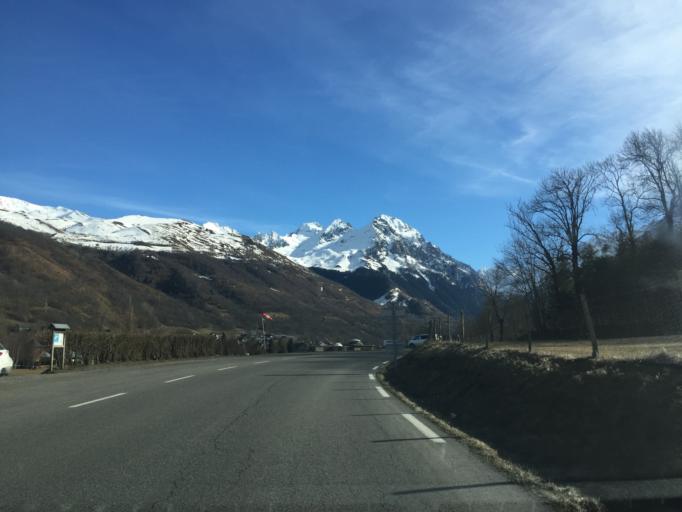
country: FR
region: Midi-Pyrenees
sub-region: Departement des Hautes-Pyrenees
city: Saint-Lary-Soulan
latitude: 42.8030
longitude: 0.4046
